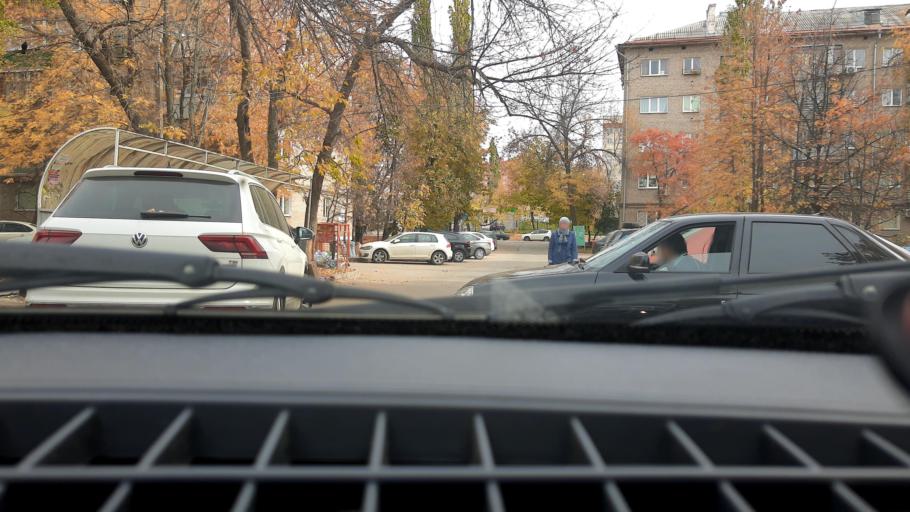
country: RU
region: Bashkortostan
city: Ufa
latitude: 54.7347
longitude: 55.9696
